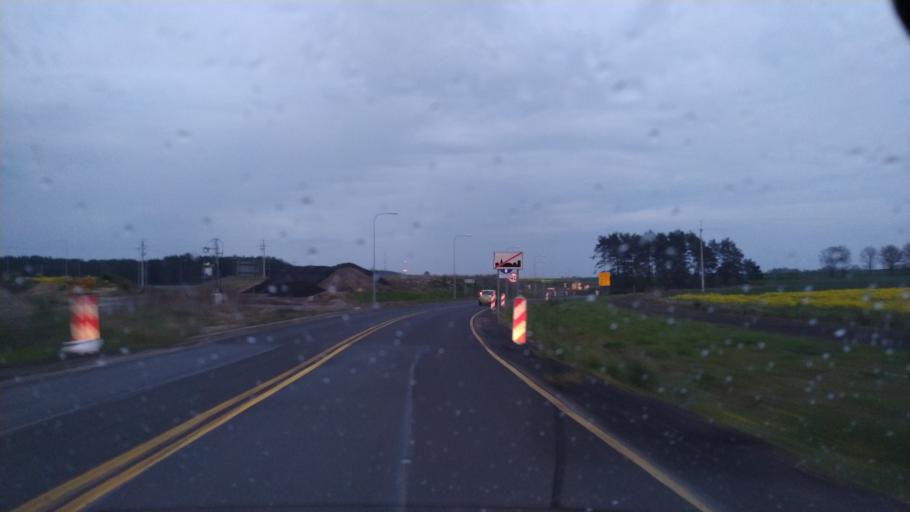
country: PL
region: Greater Poland Voivodeship
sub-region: Powiat pilski
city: Szydlowo
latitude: 53.2465
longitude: 16.5983
